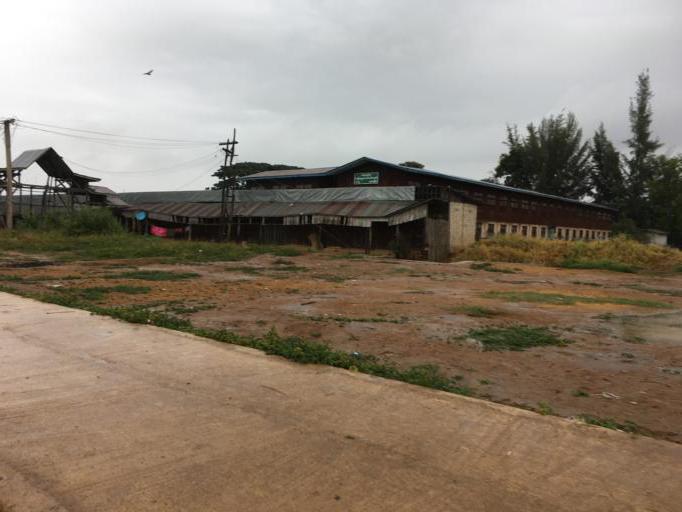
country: MM
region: Shan
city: Taunggyi
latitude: 20.4743
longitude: 96.8916
